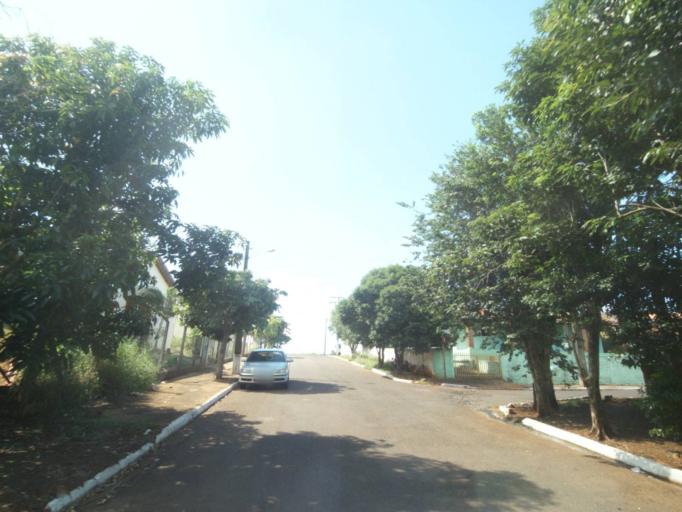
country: BR
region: Parana
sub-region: Sertanopolis
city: Sertanopolis
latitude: -23.0459
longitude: -50.8238
